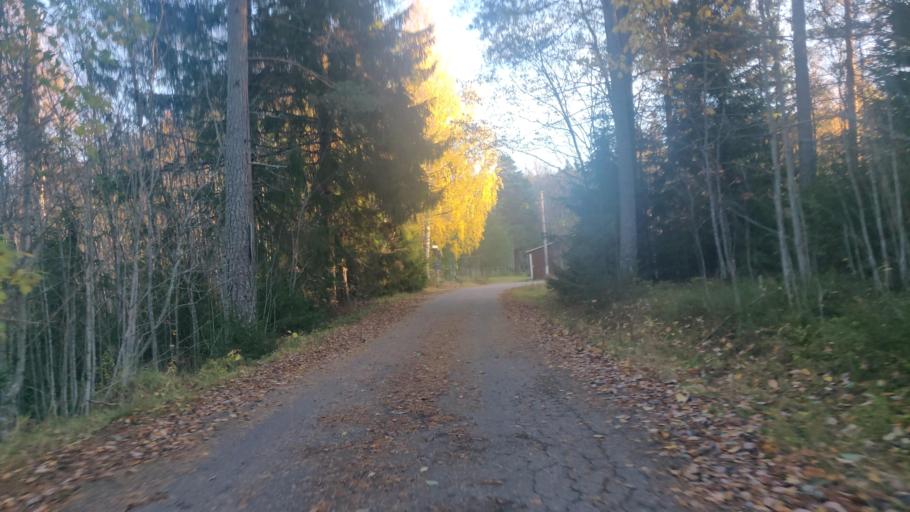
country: SE
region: Vaesternorrland
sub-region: Sundsvalls Kommun
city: Njurundabommen
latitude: 62.2685
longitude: 17.3991
